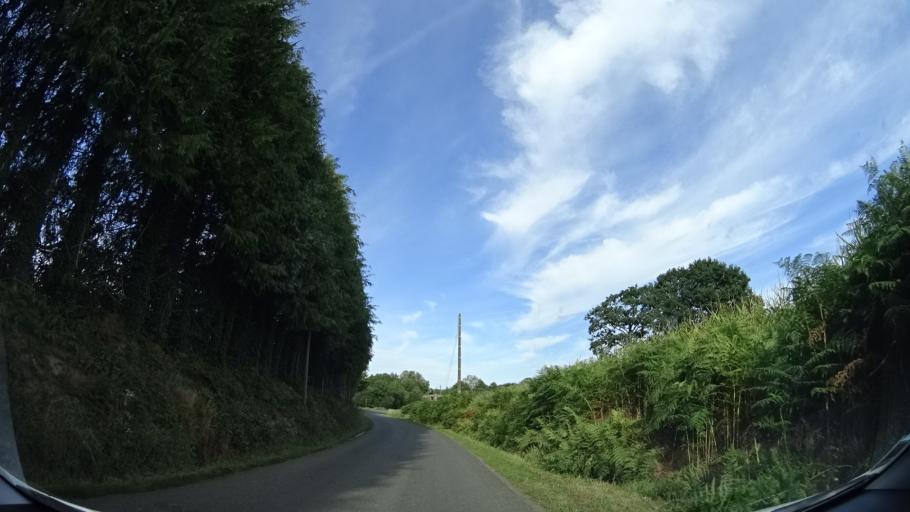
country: FR
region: Brittany
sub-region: Departement d'Ille-et-Vilaine
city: Javene
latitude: 48.3412
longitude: -1.2253
